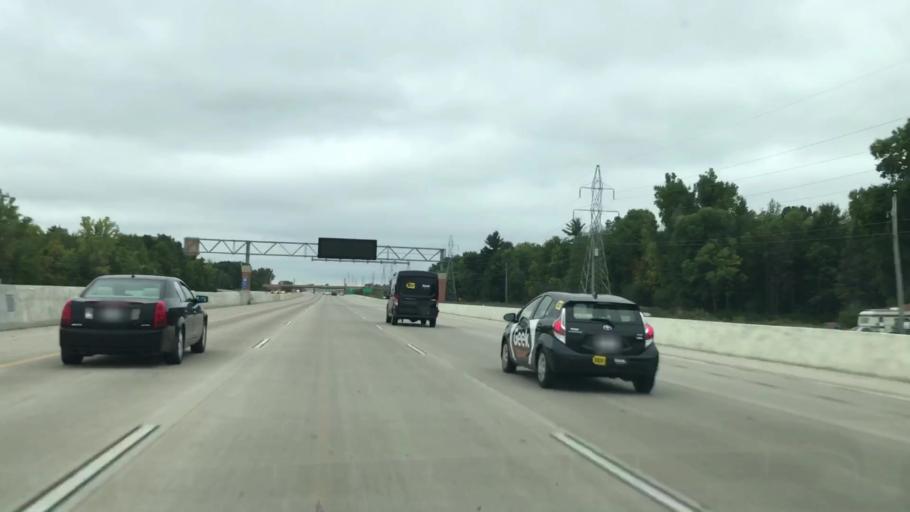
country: US
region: Wisconsin
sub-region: Brown County
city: Suamico
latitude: 44.5836
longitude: -88.0487
